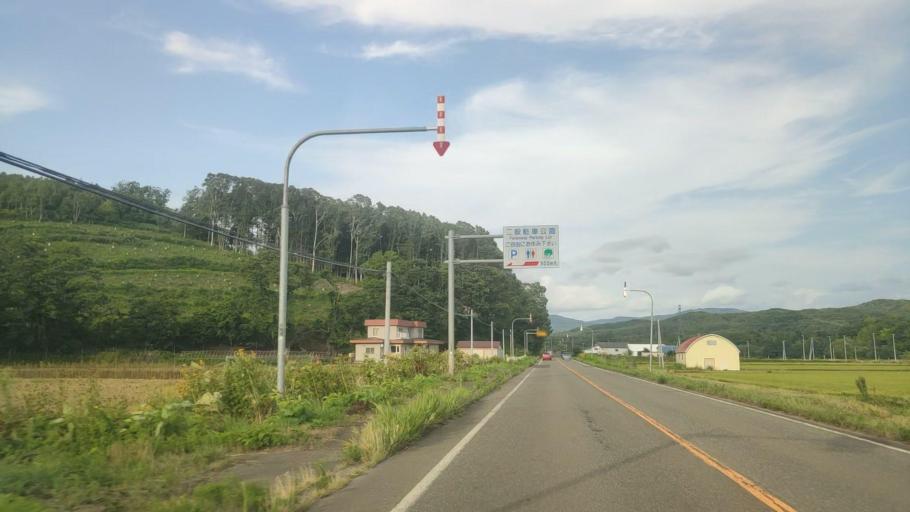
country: JP
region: Hokkaido
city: Iwamizawa
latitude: 43.0260
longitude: 141.8767
